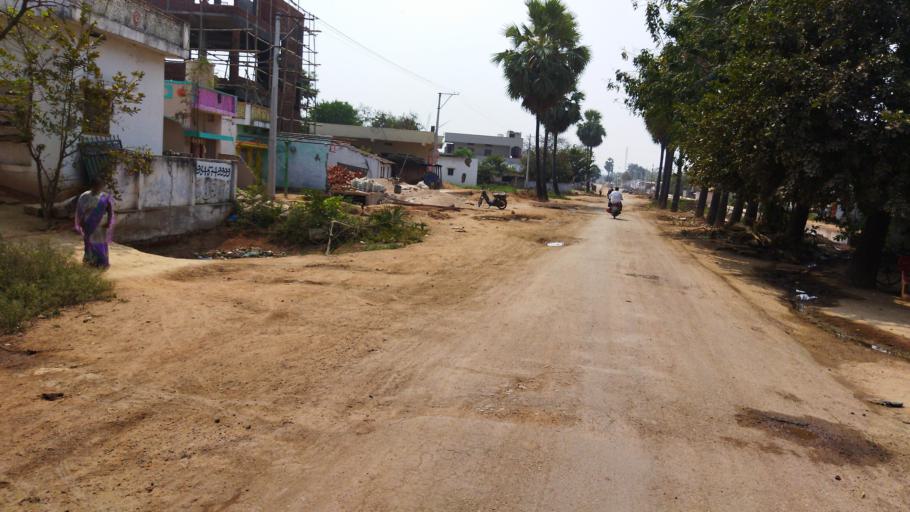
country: IN
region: Telangana
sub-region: Nalgonda
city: Nalgonda
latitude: 17.1259
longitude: 79.3686
